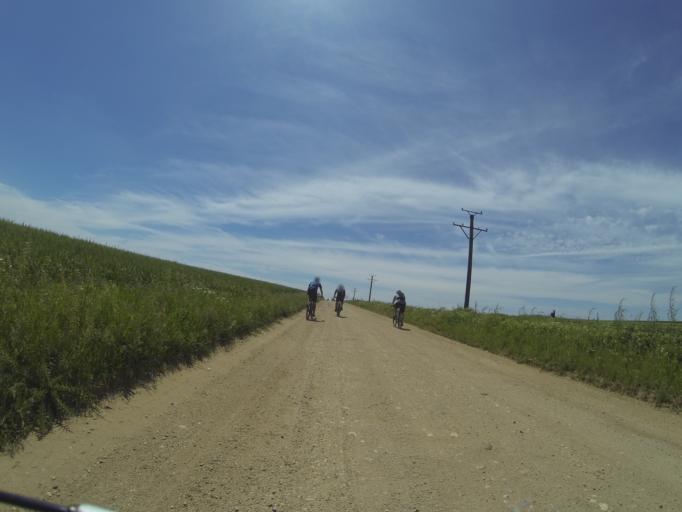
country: RO
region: Dolj
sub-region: Comuna Leu
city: Zanoaga
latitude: 44.1704
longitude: 24.0912
